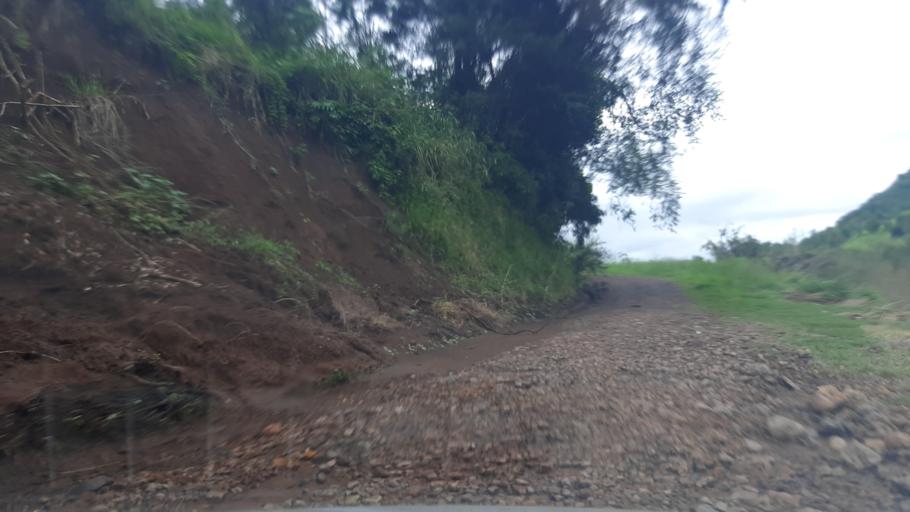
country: BR
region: Parana
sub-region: Ampere
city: Ampere
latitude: -26.0472
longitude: -53.5177
